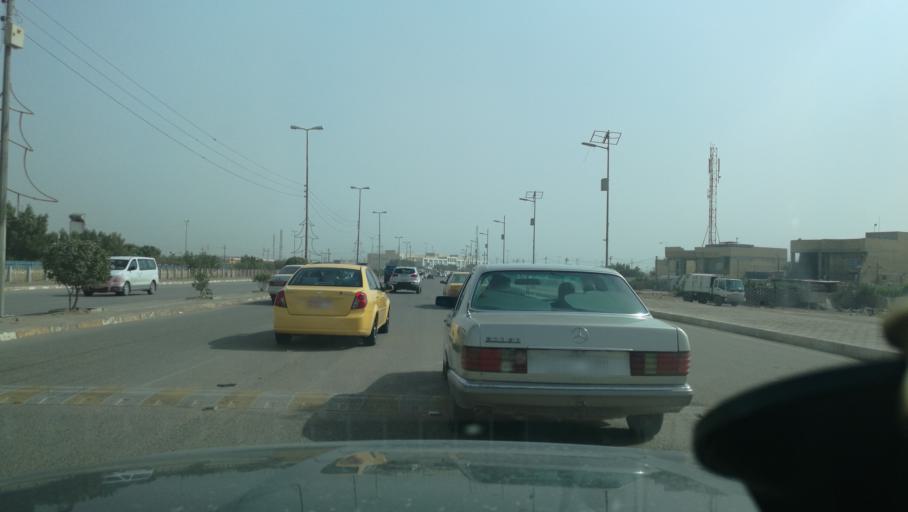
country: IQ
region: Dhi Qar
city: An Nasiriyah
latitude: 31.0849
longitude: 46.2446
